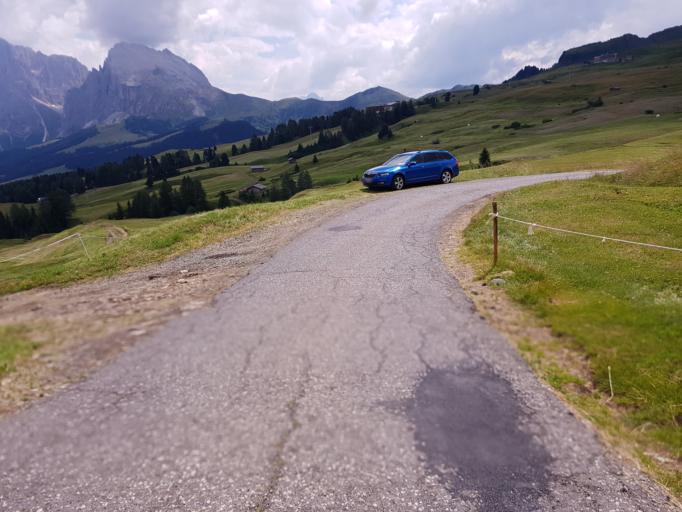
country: IT
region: Trentino-Alto Adige
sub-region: Bolzano
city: Ortisei
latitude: 46.5309
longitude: 11.6306
